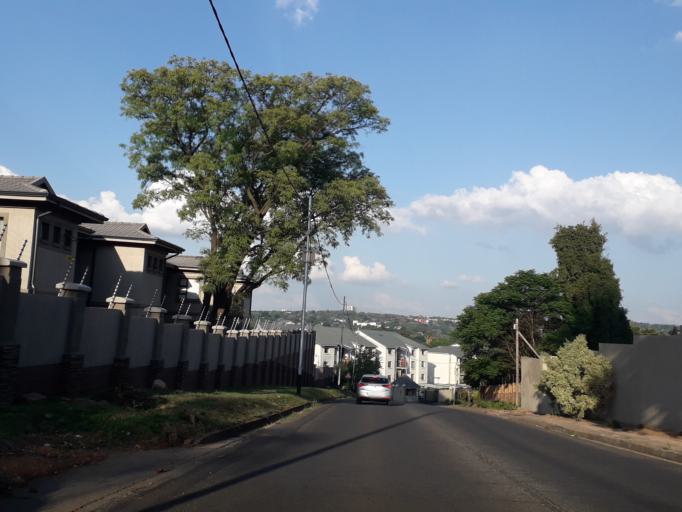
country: ZA
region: Gauteng
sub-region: City of Johannesburg Metropolitan Municipality
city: Johannesburg
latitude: -26.1371
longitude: 28.0052
